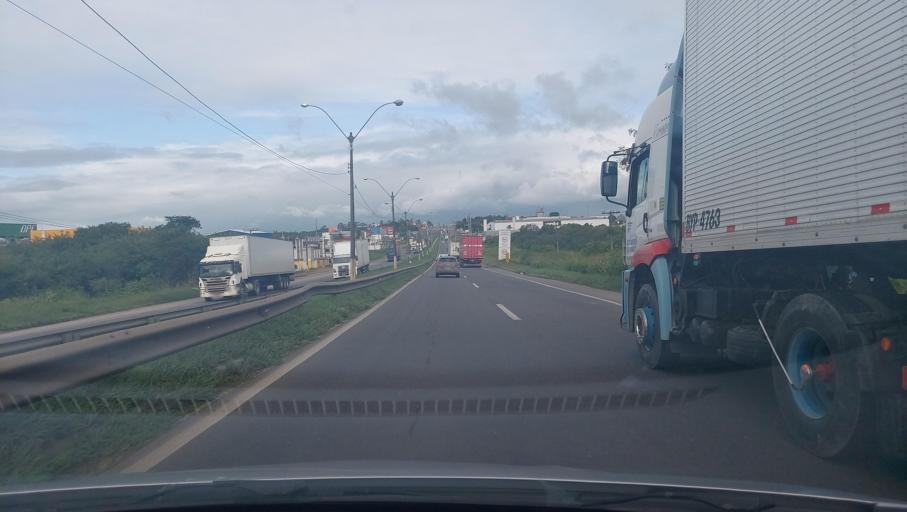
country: BR
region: Bahia
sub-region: Feira De Santana
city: Feira de Santana
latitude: -12.2854
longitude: -38.9190
